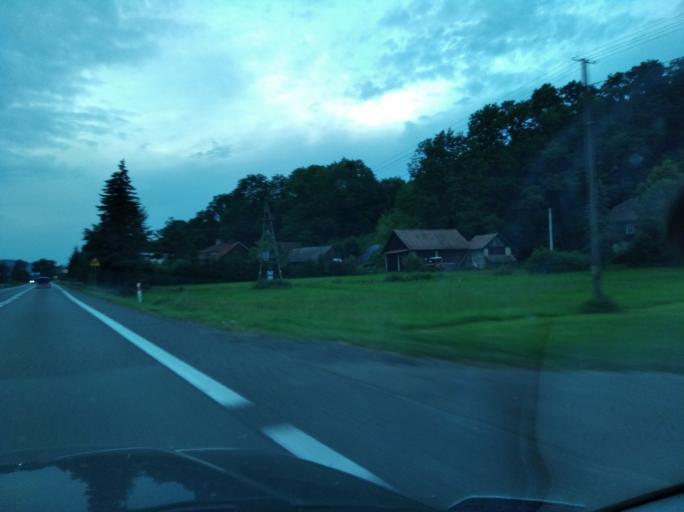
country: PL
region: Subcarpathian Voivodeship
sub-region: Powiat brzozowski
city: Domaradz
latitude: 49.8033
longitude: 21.9181
